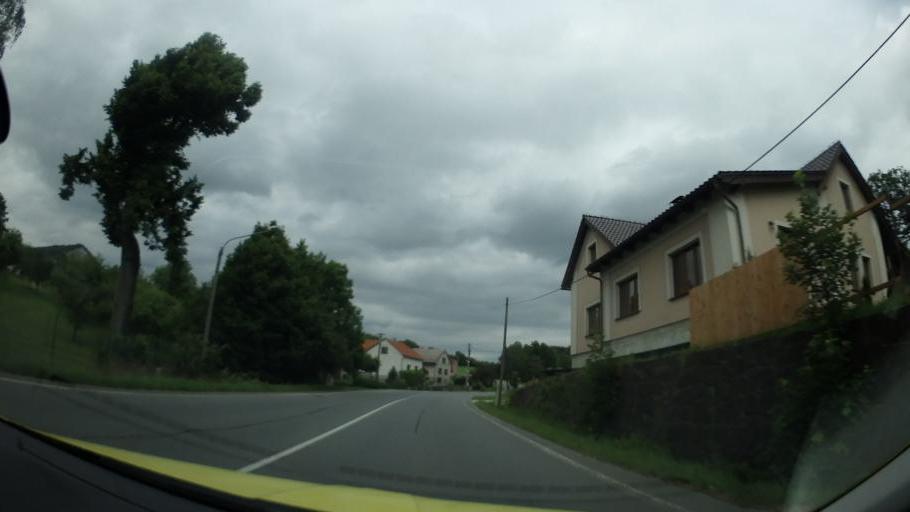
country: CZ
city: Stramberk
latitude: 49.5731
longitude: 18.1095
